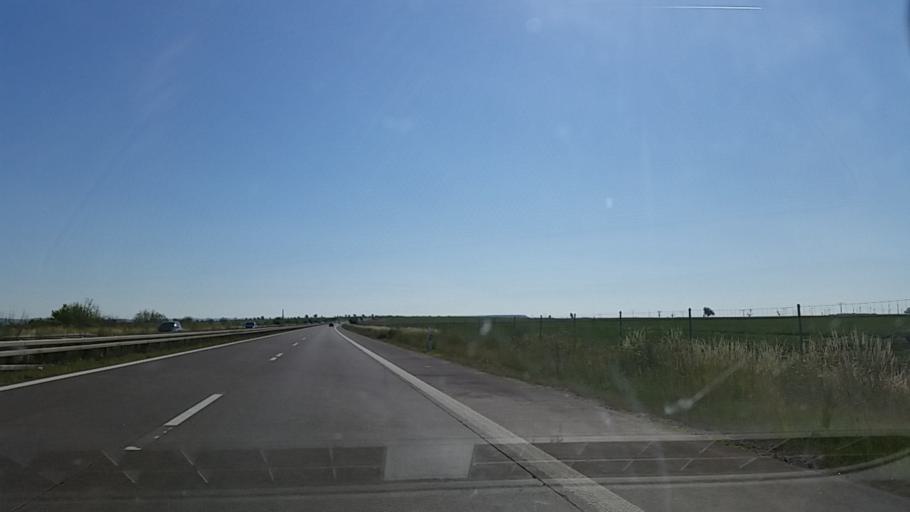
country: DE
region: Saxony-Anhalt
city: Gatersleben
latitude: 51.8021
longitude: 11.2505
